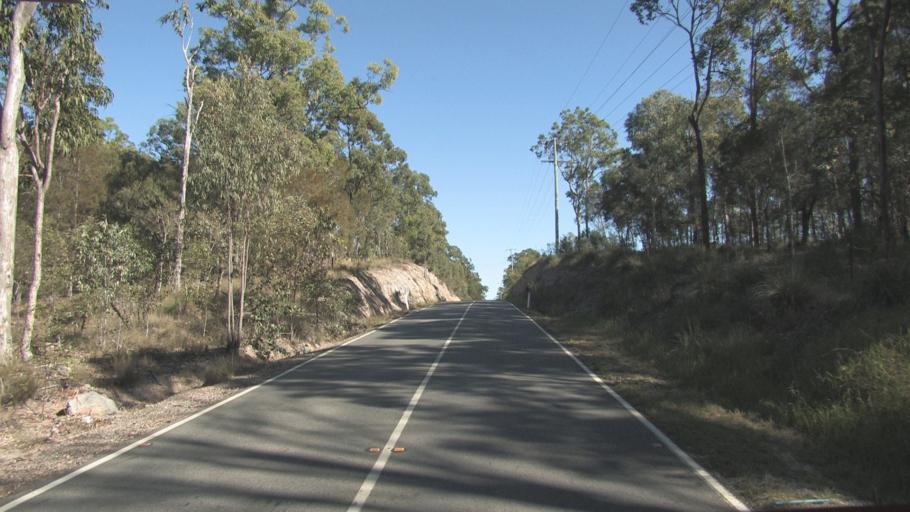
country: AU
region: Queensland
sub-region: Ipswich
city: Springfield Lakes
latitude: -27.6988
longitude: 152.9682
